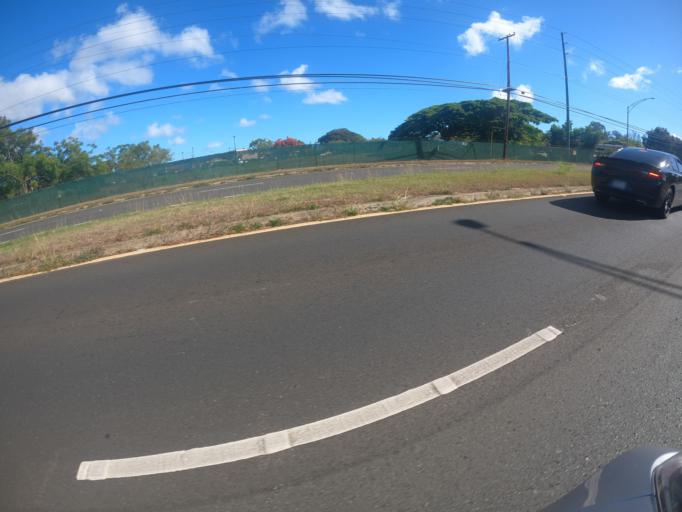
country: US
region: Hawaii
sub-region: Honolulu County
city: Schofield Barracks
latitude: 21.4838
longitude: -158.0462
